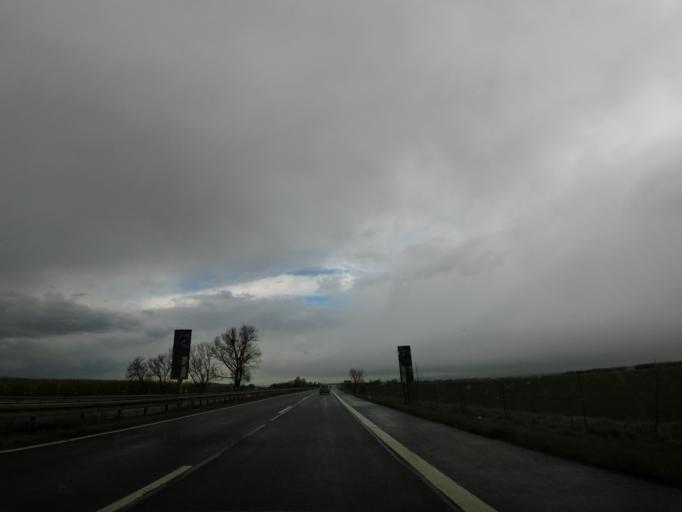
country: DE
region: Lower Saxony
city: Vienenburg
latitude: 51.9258
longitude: 10.5601
